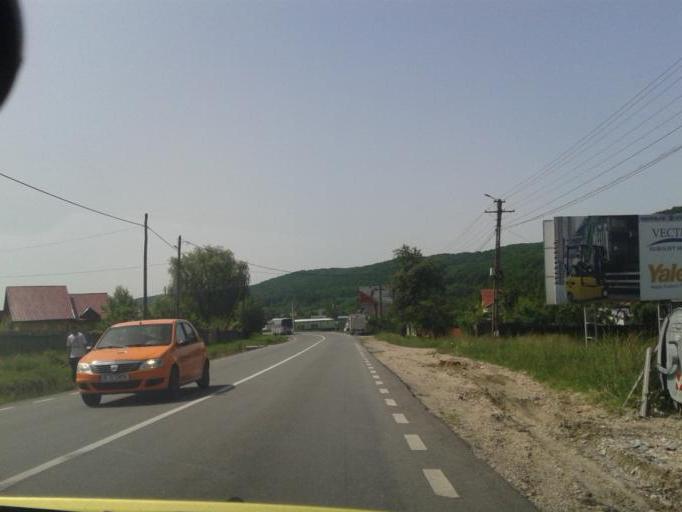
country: RO
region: Arges
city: Draganu-Olteni
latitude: 44.9153
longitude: 24.7208
